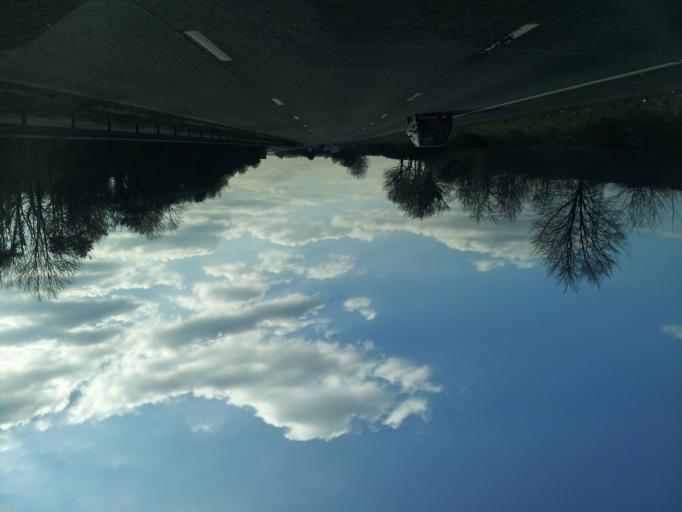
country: GB
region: England
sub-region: Somerset
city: North Petherton
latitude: 51.0815
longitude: -3.0070
